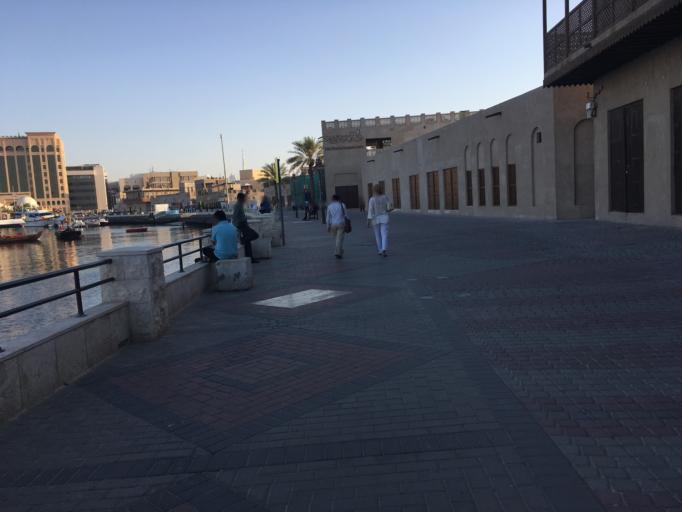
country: AE
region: Ash Shariqah
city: Sharjah
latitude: 25.2677
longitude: 55.2903
